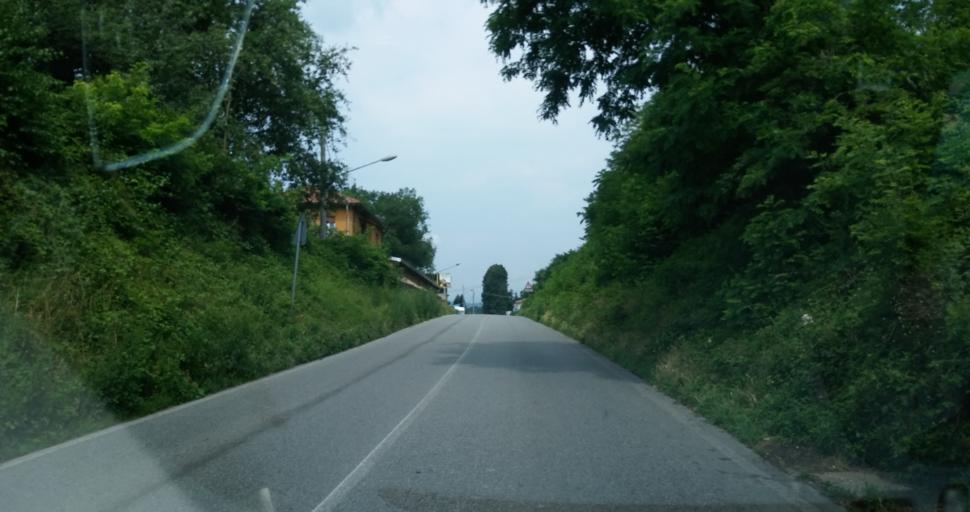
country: IT
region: Lombardy
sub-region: Provincia di Varese
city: Bardello
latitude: 45.8395
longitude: 8.6986
